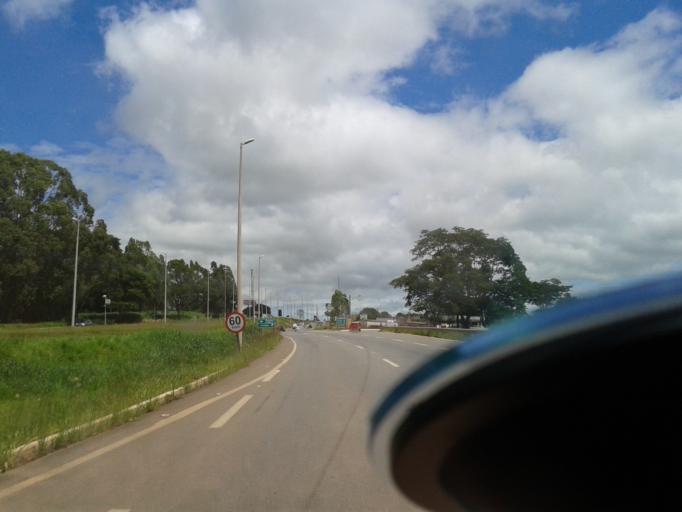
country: BR
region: Goias
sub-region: Inhumas
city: Inhumas
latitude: -16.3910
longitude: -49.4949
